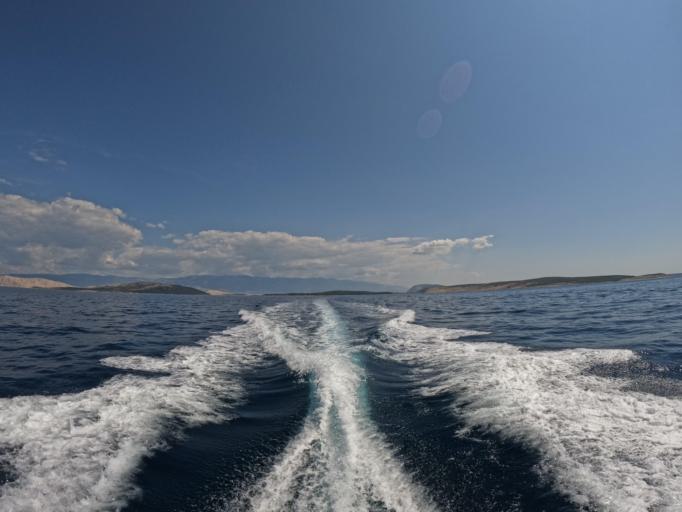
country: HR
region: Primorsko-Goranska
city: Lopar
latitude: 44.8668
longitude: 14.6816
